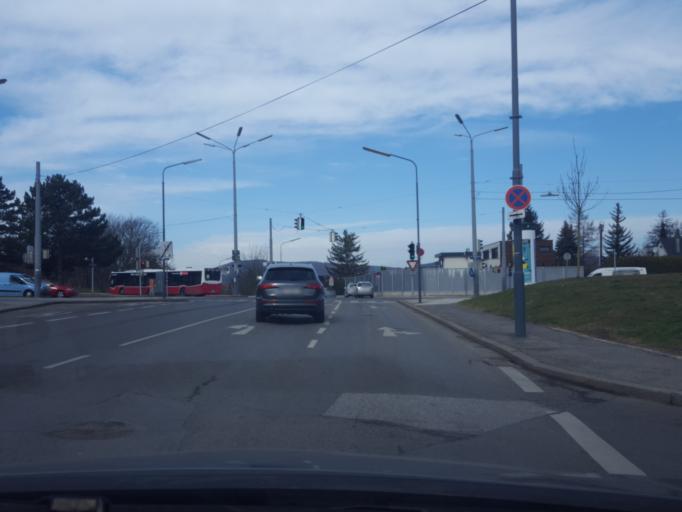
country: AT
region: Lower Austria
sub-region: Politischer Bezirk Modling
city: Perchtoldsdorf
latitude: 48.1622
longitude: 16.2924
